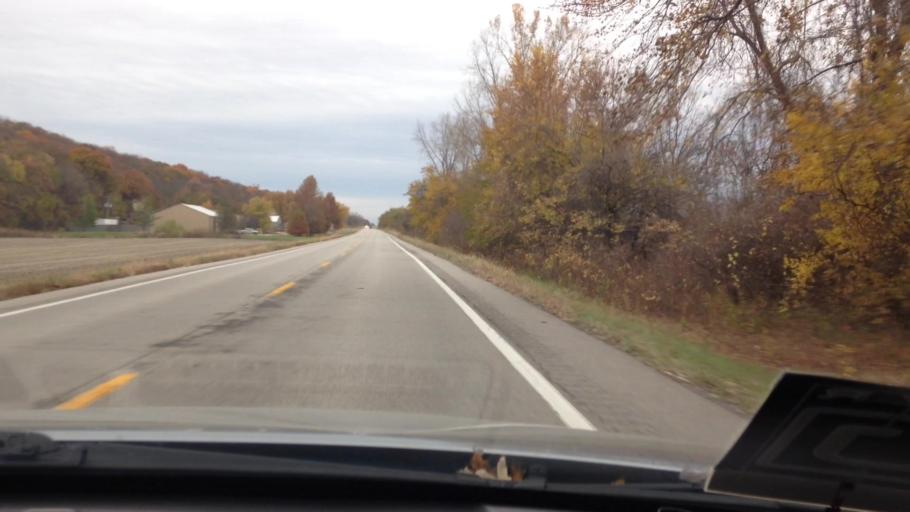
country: US
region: Kansas
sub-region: Leavenworth County
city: Leavenworth
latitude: 39.3383
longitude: -94.8613
